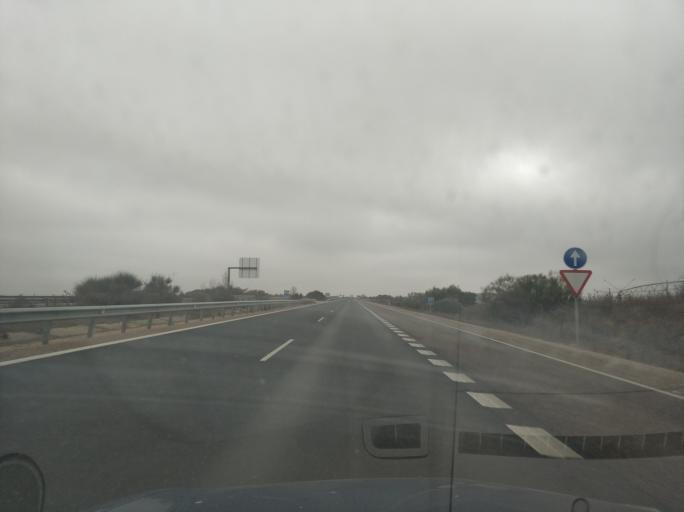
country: ES
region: Castille and Leon
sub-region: Provincia de Zamora
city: Castrillo de la Guarena
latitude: 41.2218
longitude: -5.3186
